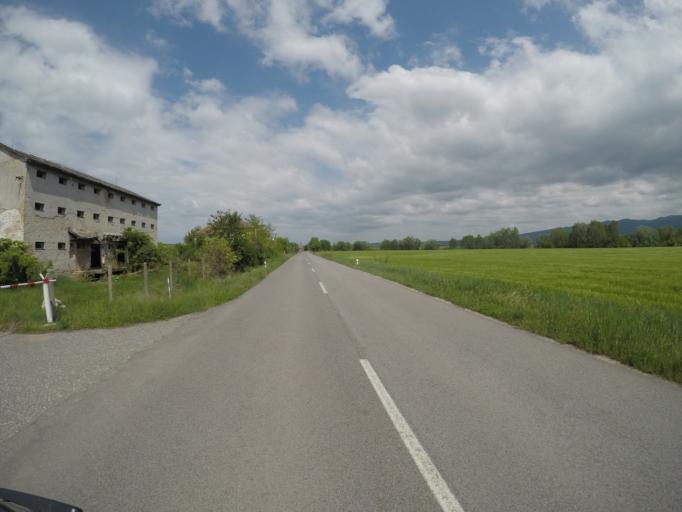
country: SK
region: Nitriansky
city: Zeliezovce
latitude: 47.9879
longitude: 18.7674
